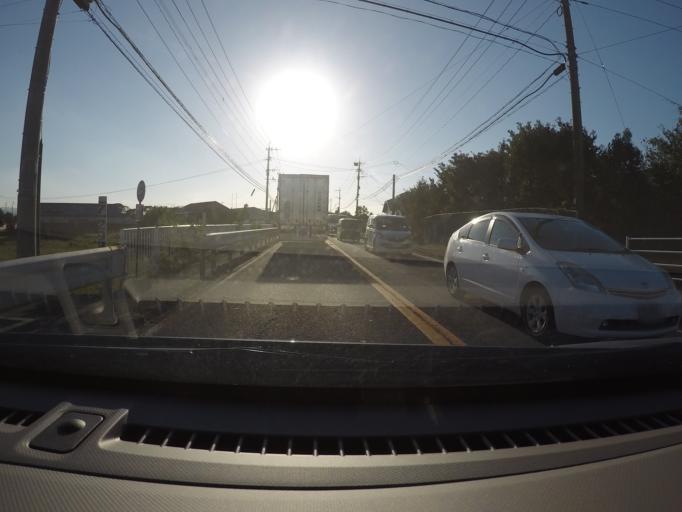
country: JP
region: Kagoshima
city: Izumi
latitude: 32.1092
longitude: 130.3250
